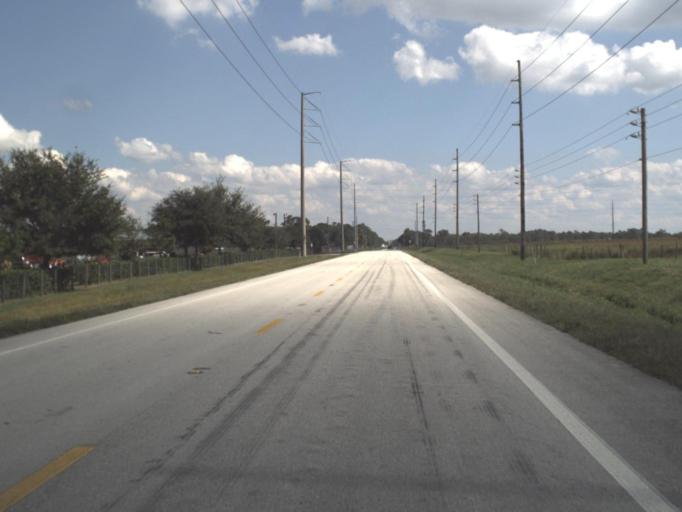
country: US
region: Florida
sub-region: Highlands County
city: Sebring
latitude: 27.4124
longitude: -81.4871
